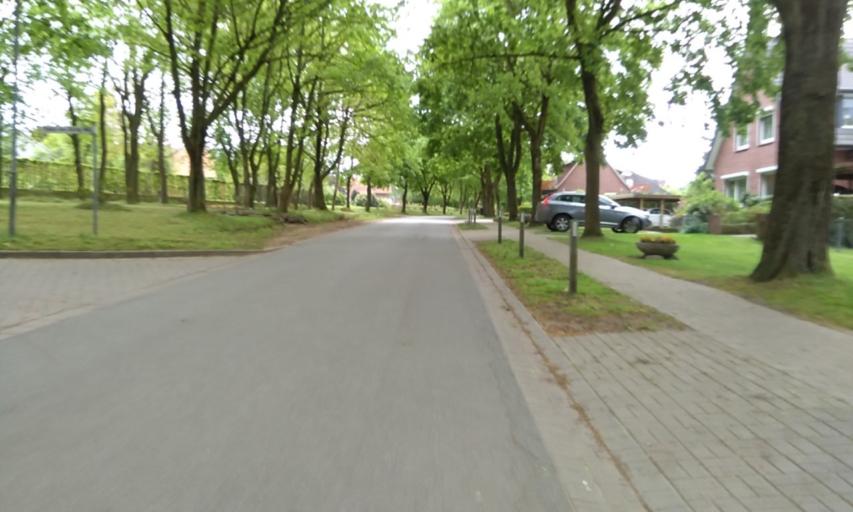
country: DE
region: Lower Saxony
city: Nottensdorf
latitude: 53.4874
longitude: 9.6059
